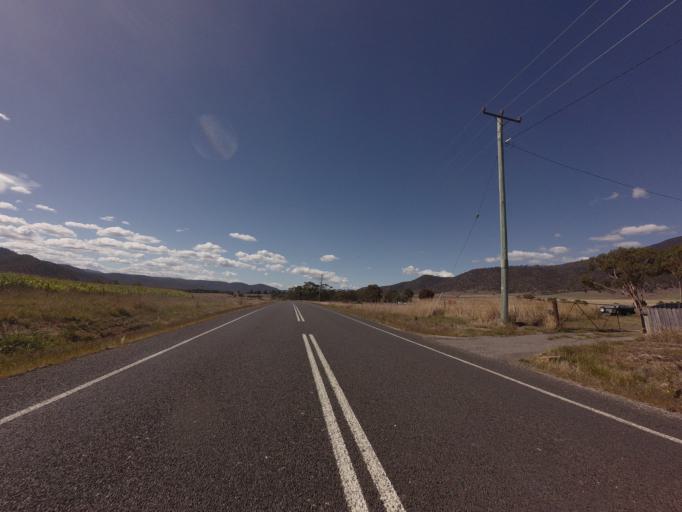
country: AU
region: Tasmania
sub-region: Break O'Day
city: St Helens
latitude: -41.7184
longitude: 147.8334
